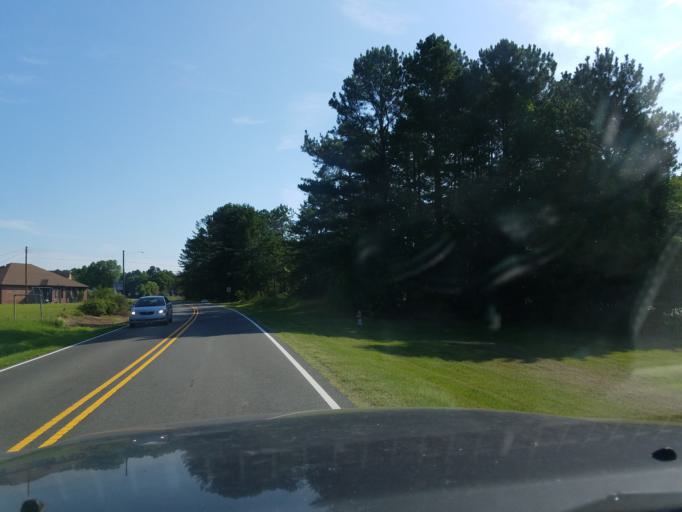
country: US
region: North Carolina
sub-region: Granville County
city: Butner
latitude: 36.1973
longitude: -78.7258
